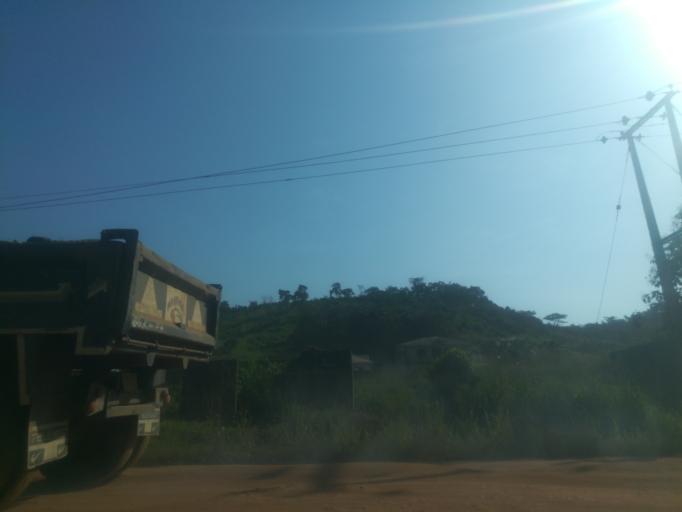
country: NG
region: Ogun
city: Abeokuta
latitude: 7.1384
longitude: 3.2779
